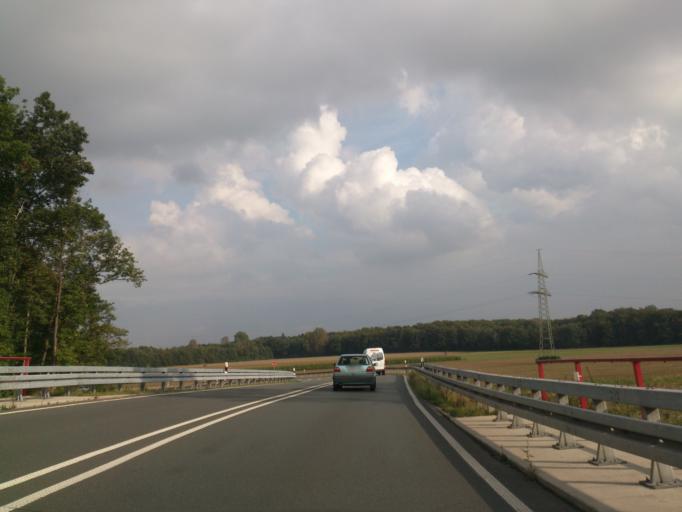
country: DE
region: North Rhine-Westphalia
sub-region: Regierungsbezirk Detmold
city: Salzkotten
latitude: 51.6854
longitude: 8.6515
